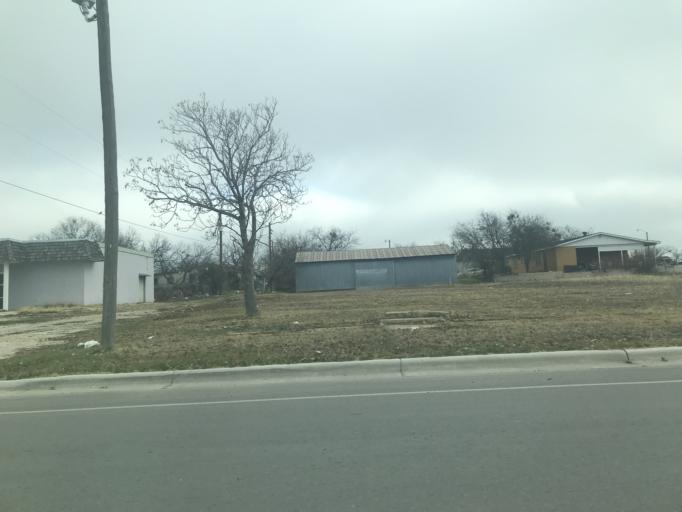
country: US
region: Texas
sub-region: Tom Green County
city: San Angelo
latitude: 31.4800
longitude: -100.4532
